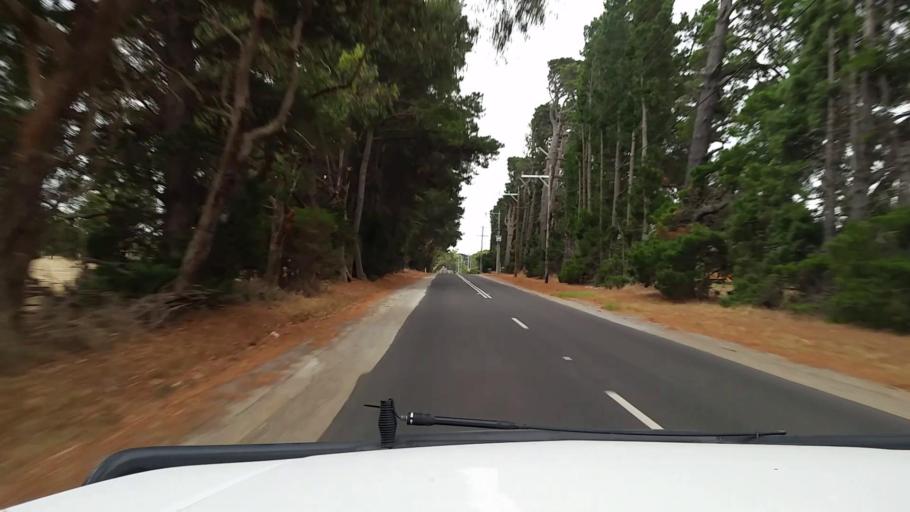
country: AU
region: Victoria
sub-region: Mornington Peninsula
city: Balnarring
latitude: -38.3362
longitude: 145.1457
